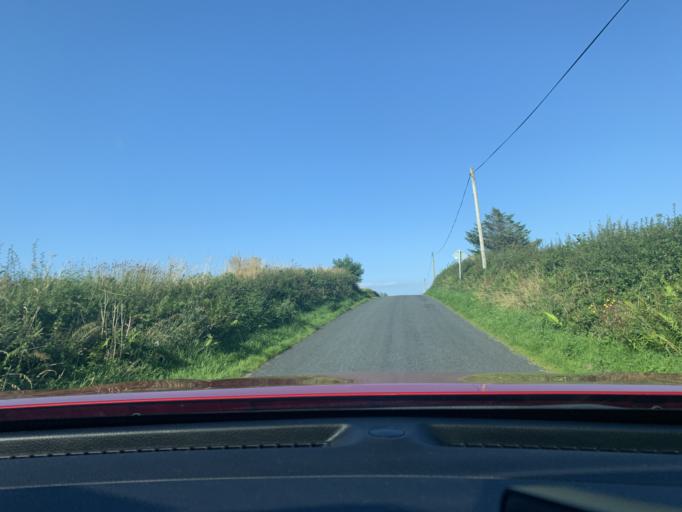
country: IE
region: Connaught
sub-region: Sligo
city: Tobercurry
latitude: 54.0828
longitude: -8.8149
